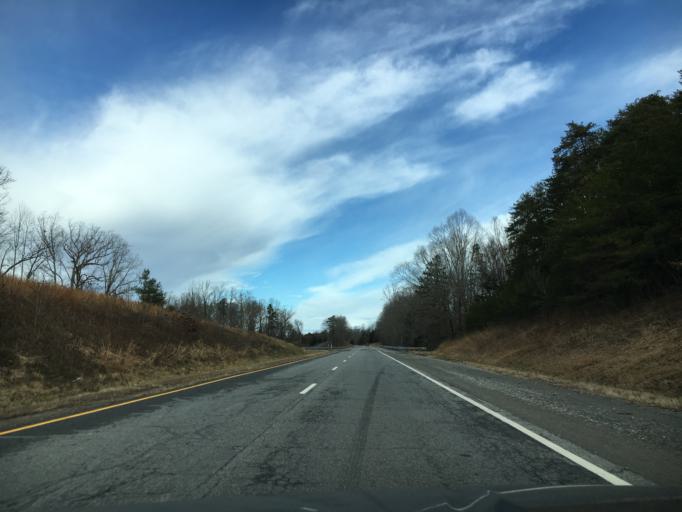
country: US
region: Virginia
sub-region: Nottoway County
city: Crewe
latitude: 37.2045
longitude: -78.2274
